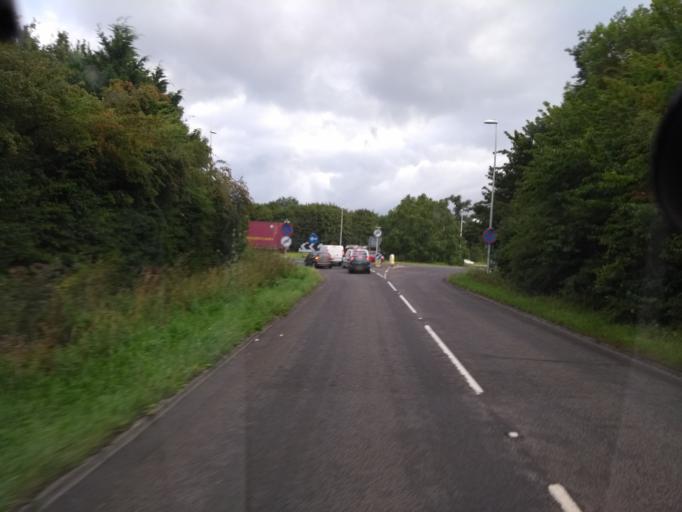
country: GB
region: England
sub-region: Somerset
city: Castle Cary
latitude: 51.0300
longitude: -2.5734
